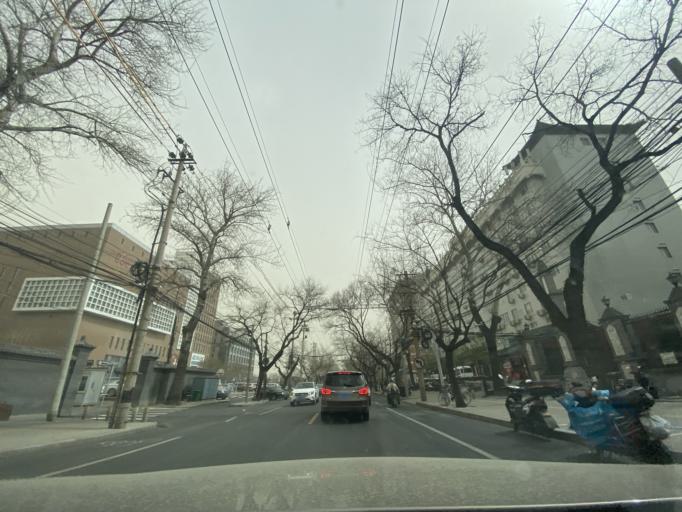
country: CN
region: Beijing
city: Jinrongjie
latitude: 39.9392
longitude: 116.3599
